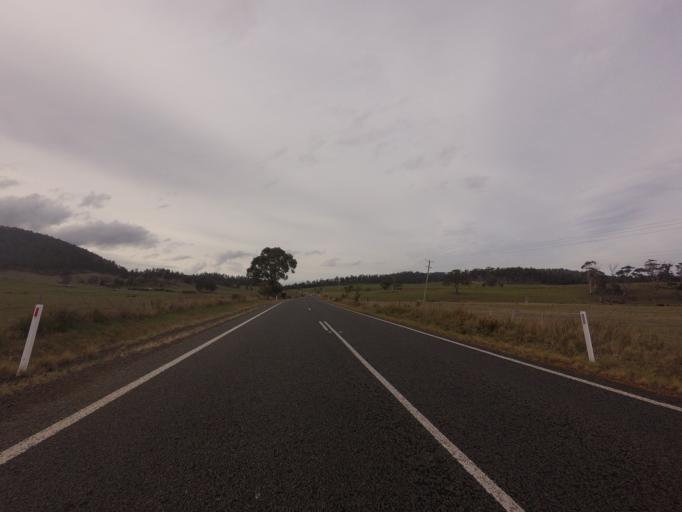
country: AU
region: Tasmania
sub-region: Sorell
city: Sorell
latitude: -42.4396
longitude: 147.9285
